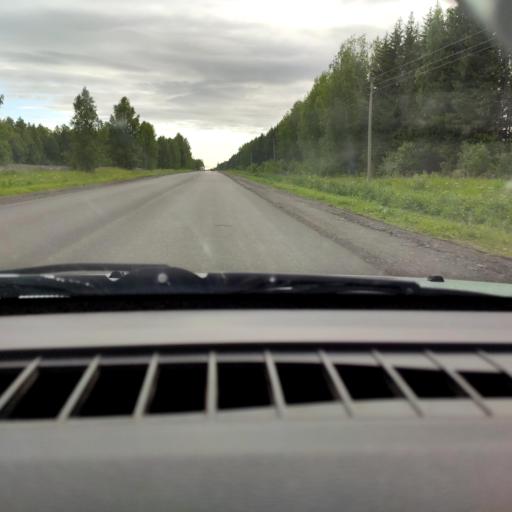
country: RU
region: Perm
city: Orda
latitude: 57.2275
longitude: 56.9625
